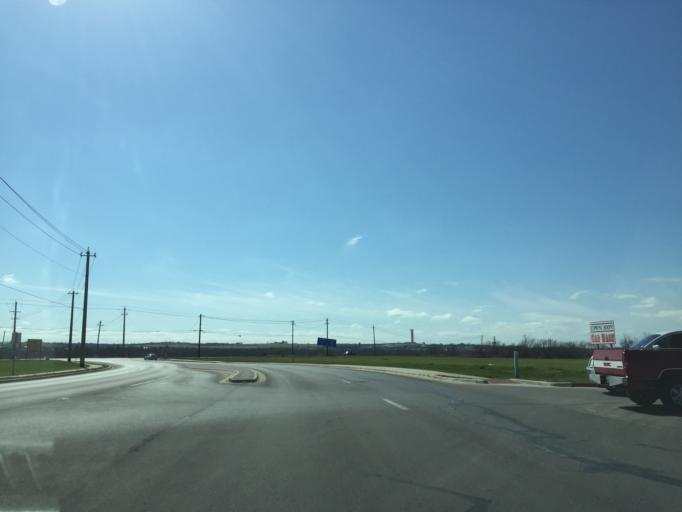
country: US
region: Texas
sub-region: Travis County
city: Garfield
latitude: 30.1553
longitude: -97.6408
